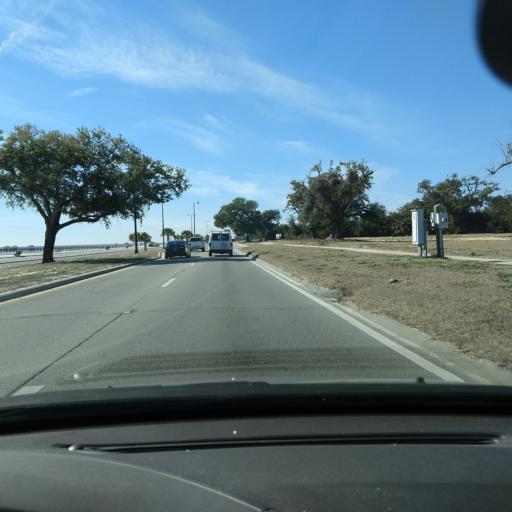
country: US
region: Mississippi
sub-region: Harrison County
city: Gulfport
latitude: 30.3616
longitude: -89.1048
